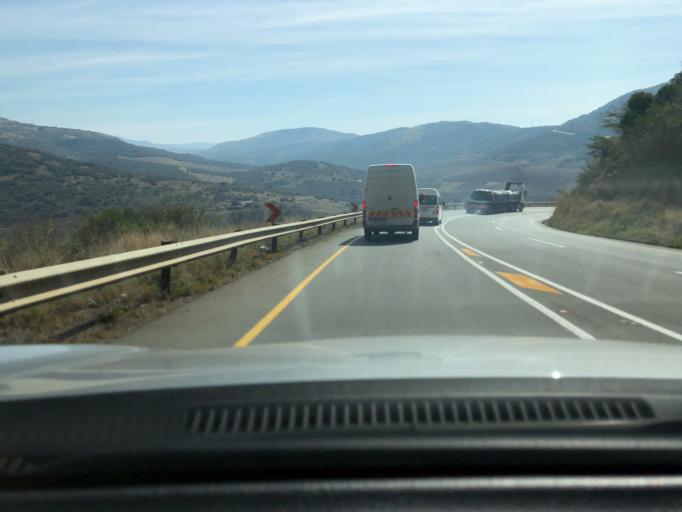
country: ZA
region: KwaZulu-Natal
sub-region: uMgungundlovu District Municipality
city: Richmond
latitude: -30.0145
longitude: 30.2383
